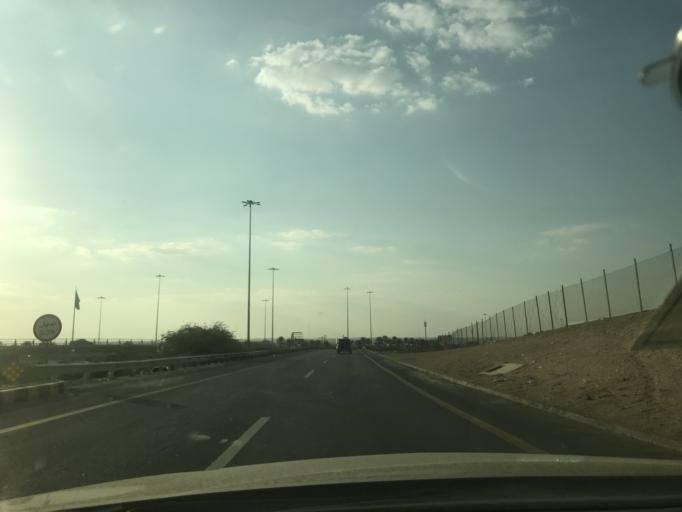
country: SA
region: Ar Riyad
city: Riyadh
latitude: 24.7386
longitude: 46.5923
